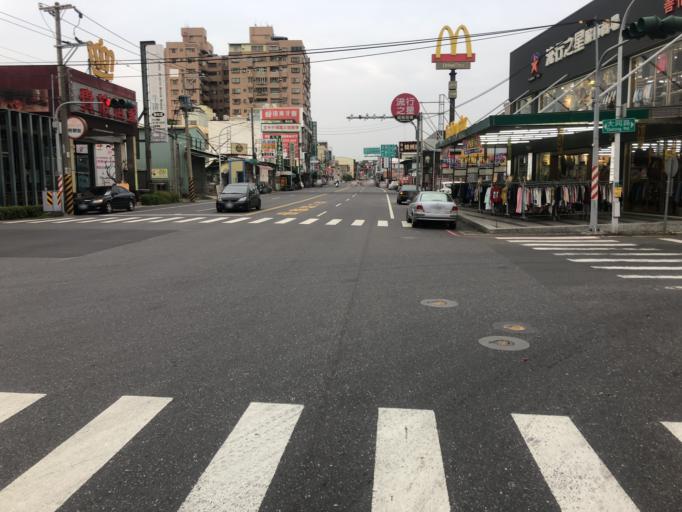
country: TW
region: Taiwan
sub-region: Tainan
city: Tainan
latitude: 23.1282
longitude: 120.2915
